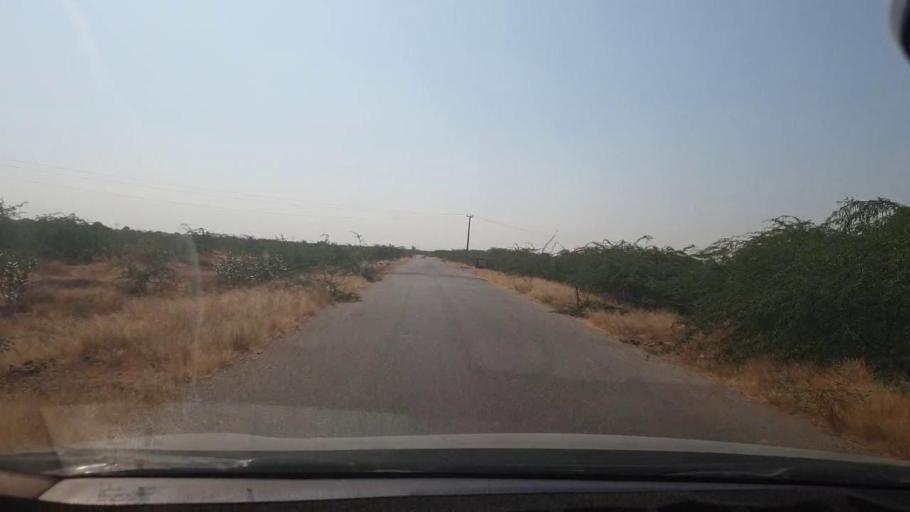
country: PK
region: Sindh
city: Malir Cantonment
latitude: 25.1611
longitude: 67.1512
